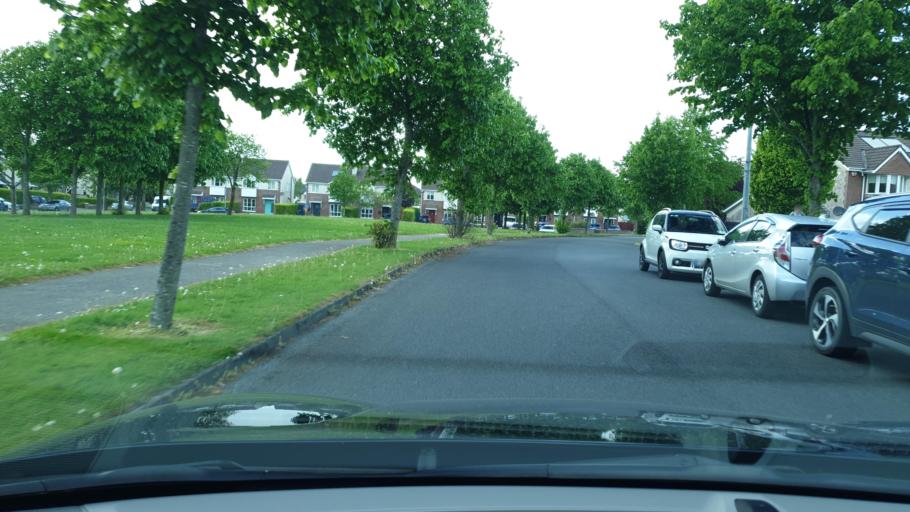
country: IE
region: Leinster
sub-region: Kildare
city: Sallins
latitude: 53.2352
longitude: -6.6547
